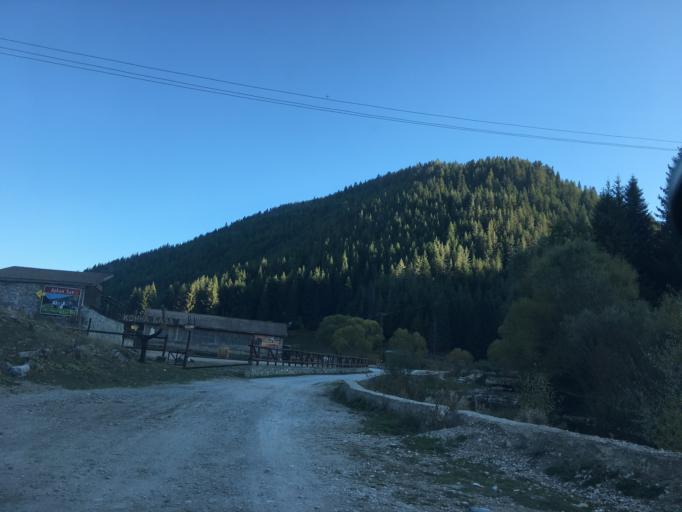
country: BG
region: Smolyan
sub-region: Obshtina Borino
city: Borino
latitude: 41.5839
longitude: 24.3928
